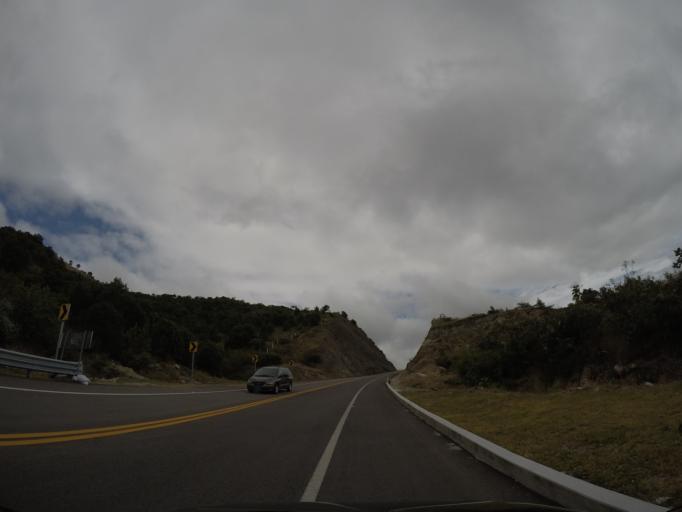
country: MX
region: Oaxaca
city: San Lorenzo Albarradas
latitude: 16.9321
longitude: -96.2671
